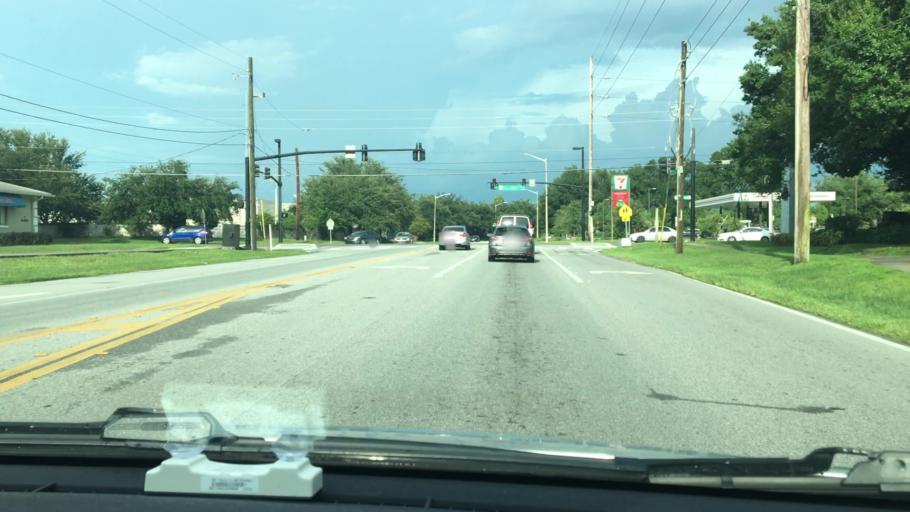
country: US
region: Florida
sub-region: Orange County
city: Conway
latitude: 28.5061
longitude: -81.3151
